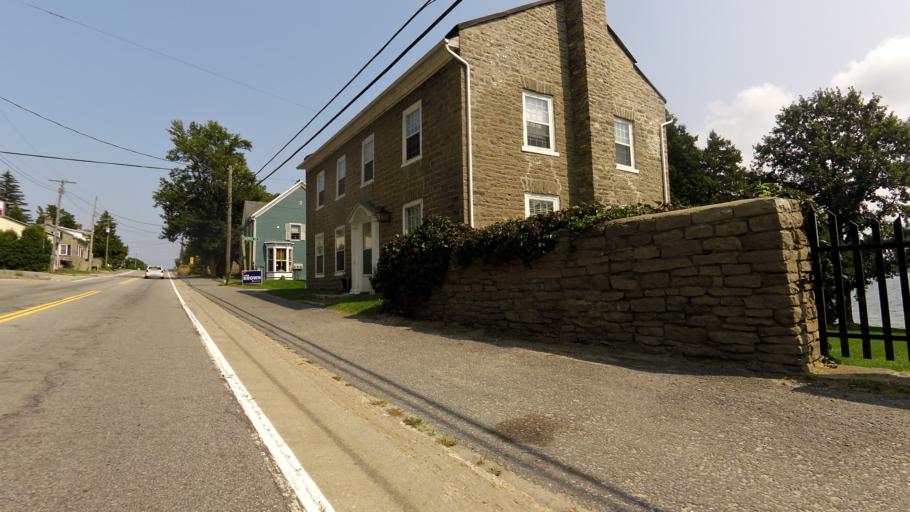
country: CA
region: Ontario
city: Brockville
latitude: 44.6358
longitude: -75.6122
